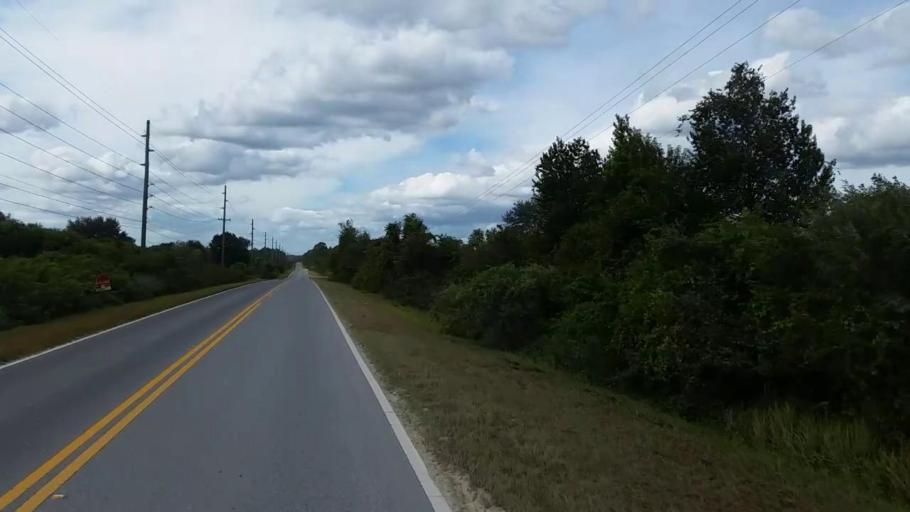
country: US
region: Florida
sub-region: Lake County
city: Four Corners
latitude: 28.3701
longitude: -81.7020
